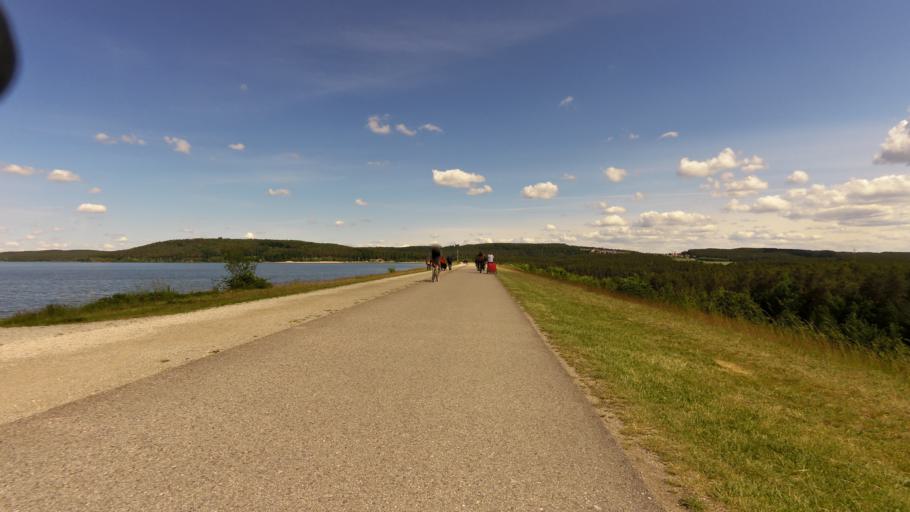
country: DE
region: Bavaria
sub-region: Regierungsbezirk Mittelfranken
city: Pleinfeld
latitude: 49.1204
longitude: 10.9647
